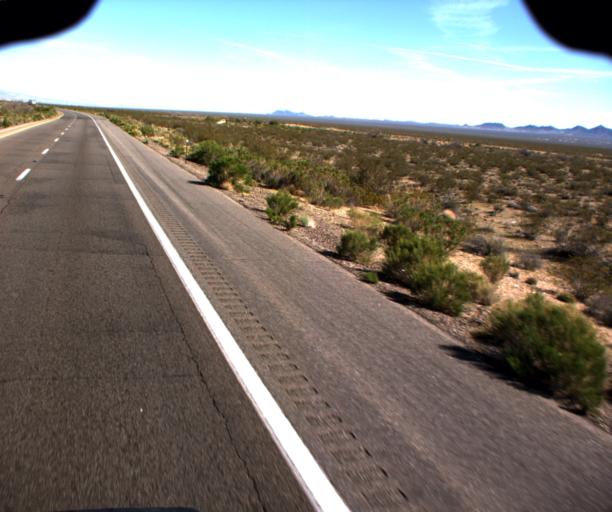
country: US
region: Arizona
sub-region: Mohave County
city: Dolan Springs
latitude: 35.6885
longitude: -114.4692
